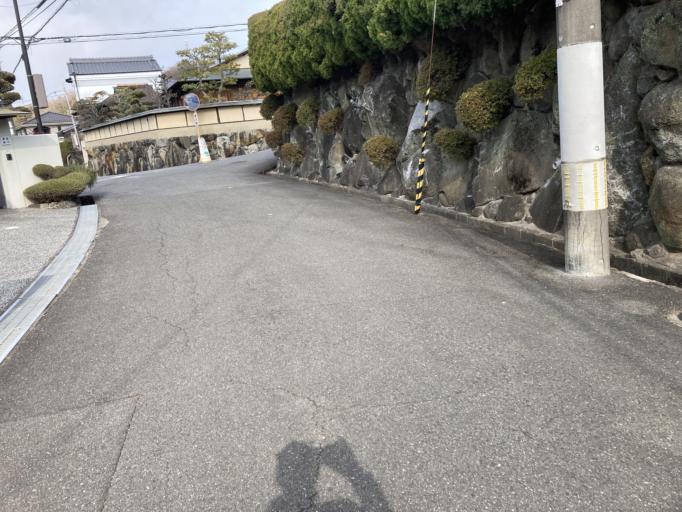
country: JP
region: Nara
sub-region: Ikoma-shi
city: Ikoma
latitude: 34.6890
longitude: 135.7117
